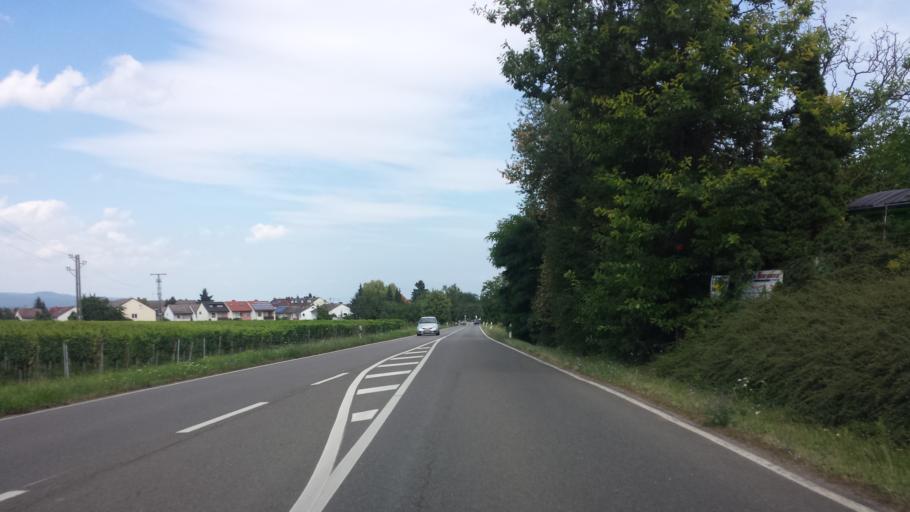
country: DE
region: Rheinland-Pfalz
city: Edenkoben
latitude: 49.2781
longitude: 8.1369
